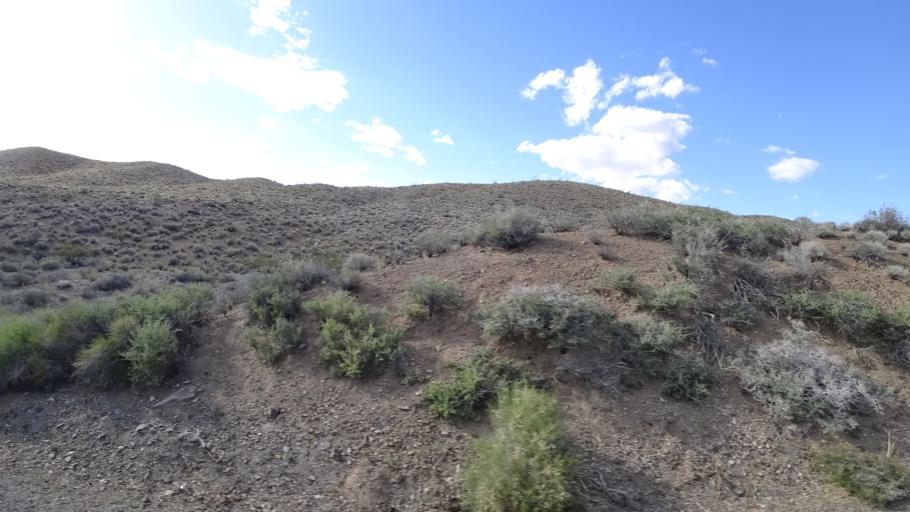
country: US
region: California
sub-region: San Bernardino County
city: Searles Valley
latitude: 36.2709
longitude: -117.1882
